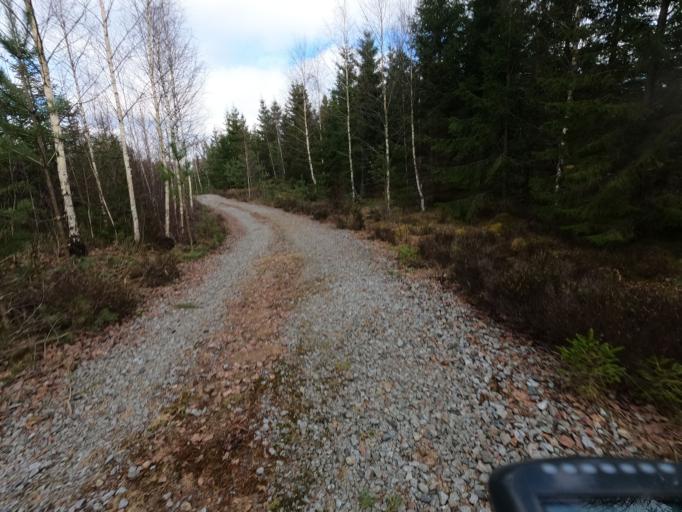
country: SE
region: Kronoberg
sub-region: Alvesta Kommun
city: Vislanda
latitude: 56.8111
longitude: 14.3986
